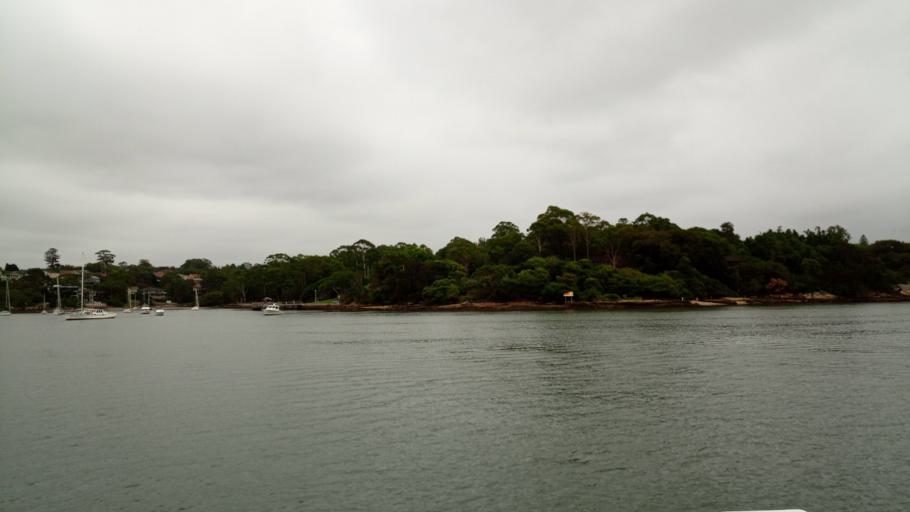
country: AU
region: New South Wales
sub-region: Hunters Hill
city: Gladesville
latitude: -33.8436
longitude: 151.1280
